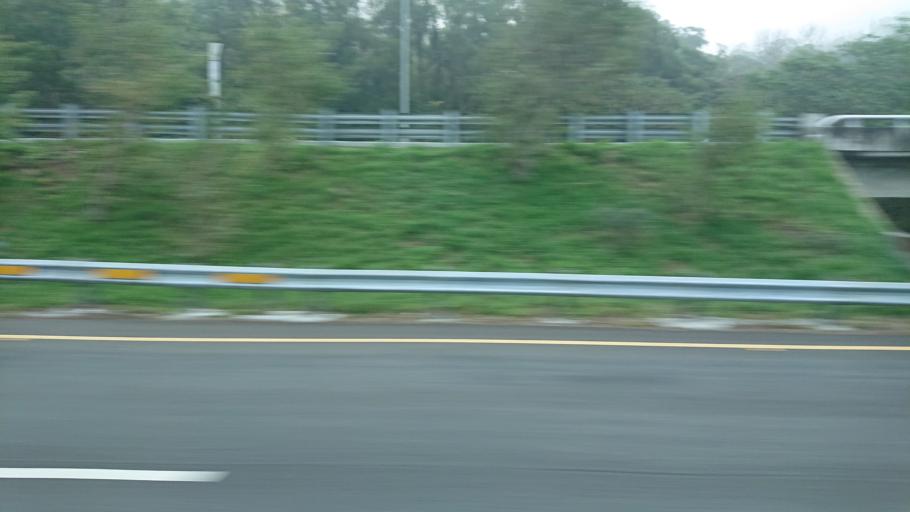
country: TW
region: Taiwan
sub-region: Miaoli
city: Miaoli
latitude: 24.4305
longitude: 120.7777
